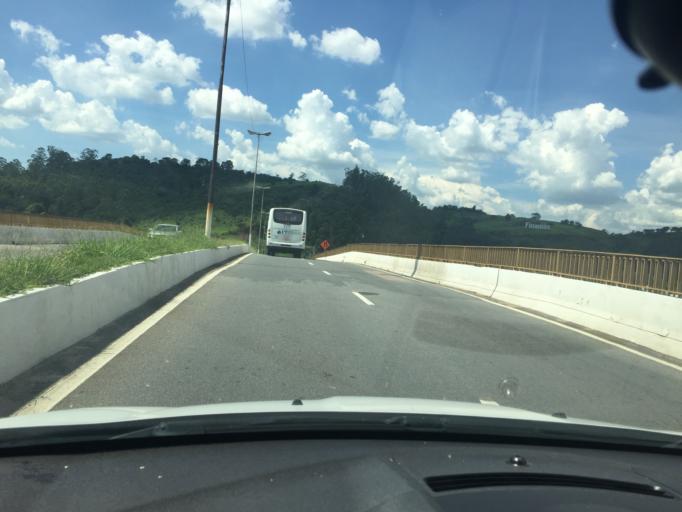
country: BR
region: Sao Paulo
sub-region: Jundiai
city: Jundiai
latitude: -23.1741
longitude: -46.8857
